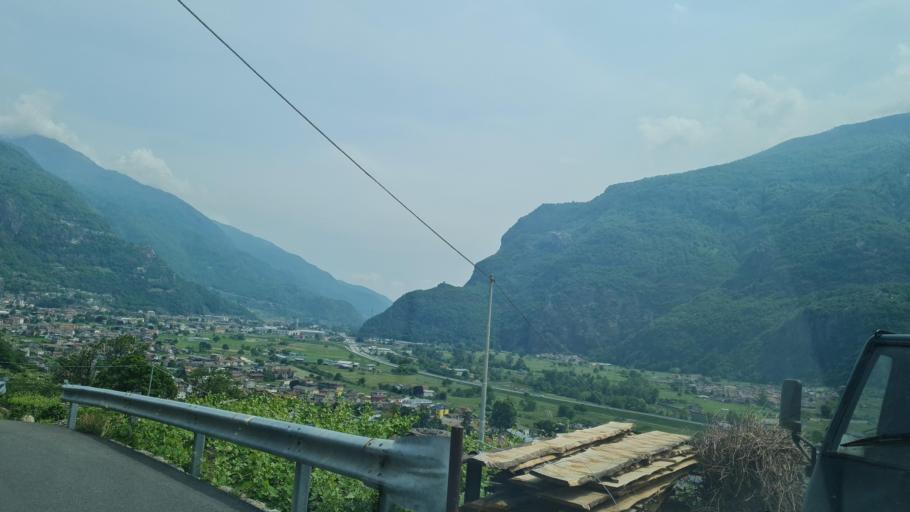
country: IT
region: Aosta Valley
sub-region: Valle d'Aosta
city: Donnas
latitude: 45.6080
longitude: 7.7693
